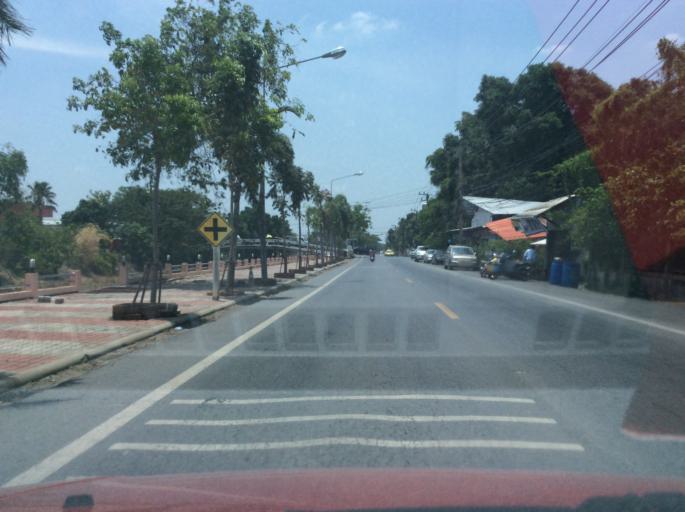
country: TH
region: Pathum Thani
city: Lam Luk Ka
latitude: 13.9637
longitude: 100.7278
